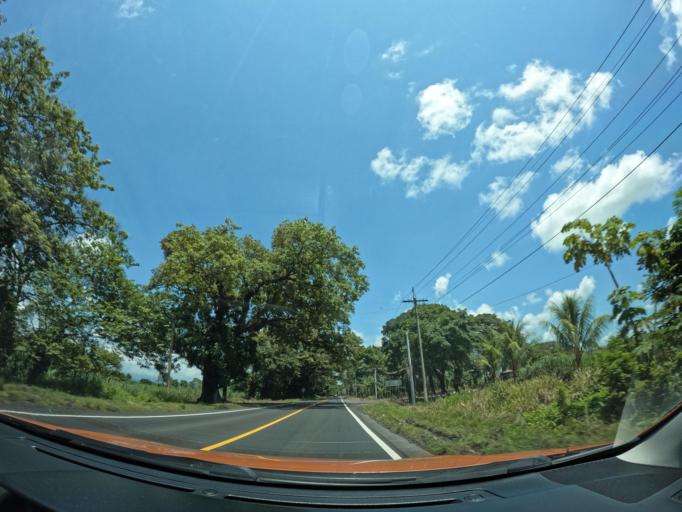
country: GT
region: Escuintla
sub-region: Municipio de Masagua
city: Masagua
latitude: 14.1818
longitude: -90.8653
